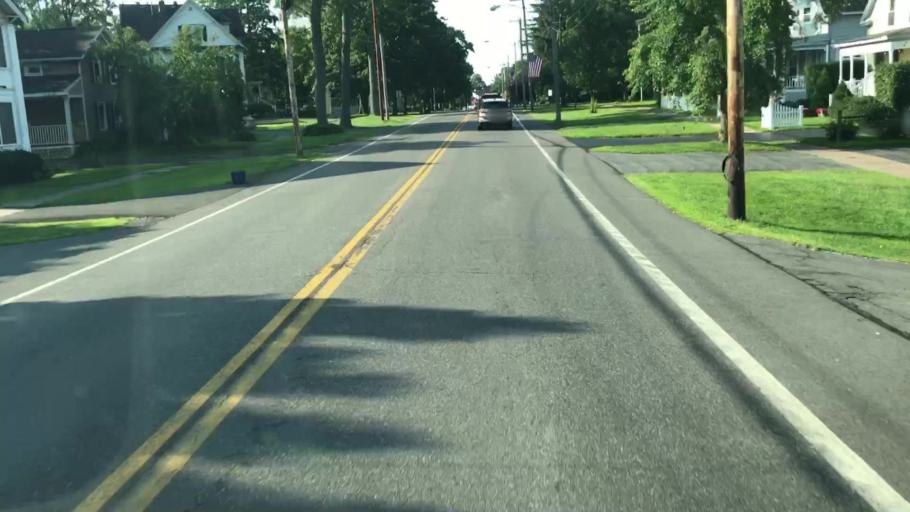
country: US
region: New York
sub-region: Onondaga County
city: Liverpool
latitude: 43.1082
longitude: -76.2064
